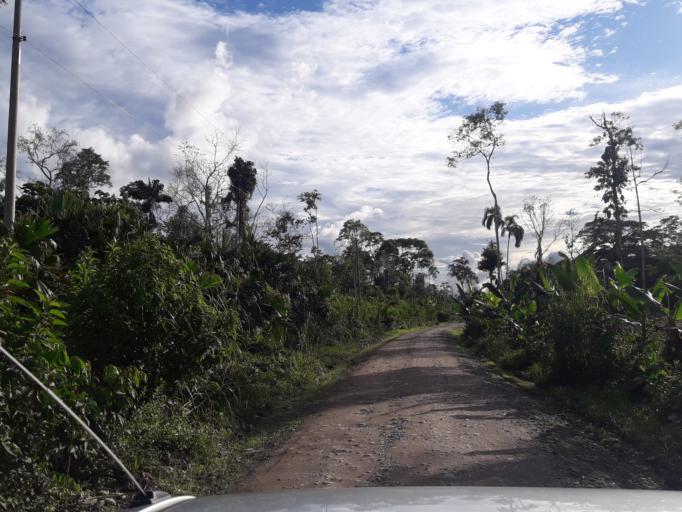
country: EC
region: Orellana
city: Boca Suno
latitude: -0.8829
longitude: -77.2876
